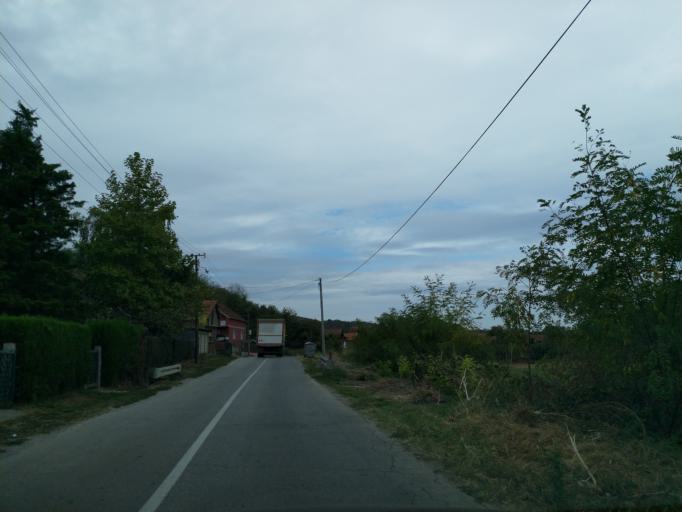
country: RS
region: Central Serbia
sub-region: Pomoravski Okrug
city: Cuprija
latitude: 43.8602
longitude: 21.3242
